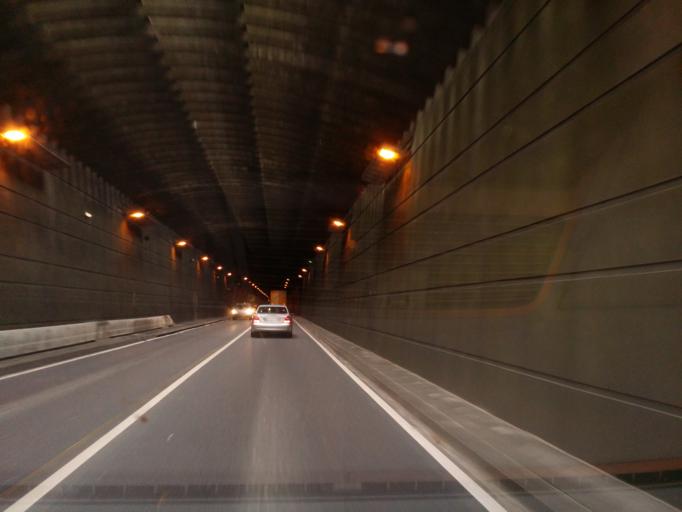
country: DE
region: Schleswig-Holstein
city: Westerronfeld
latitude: 54.2926
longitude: 9.6548
